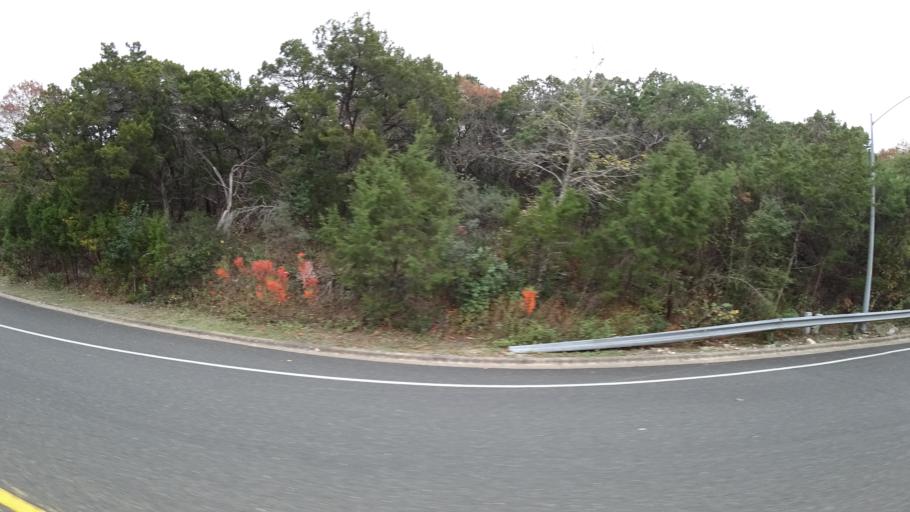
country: US
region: Texas
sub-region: Williamson County
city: Jollyville
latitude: 30.3824
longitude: -97.7894
